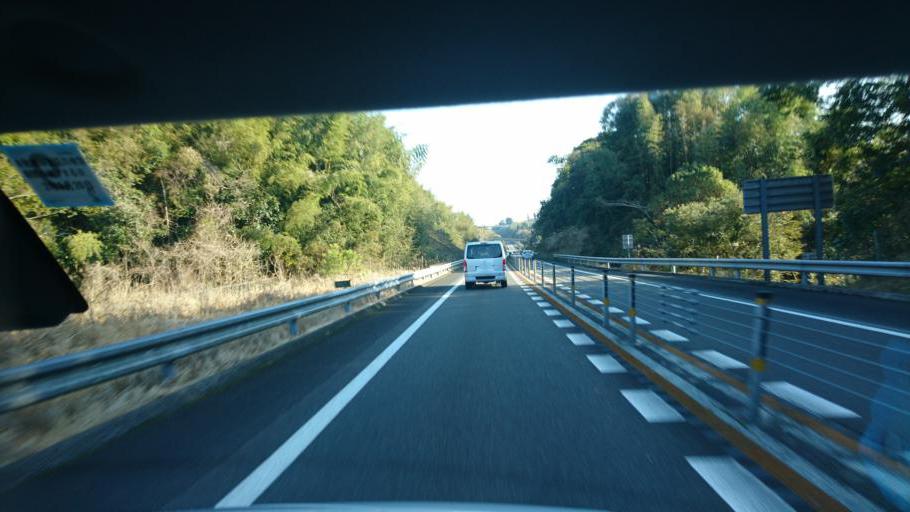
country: JP
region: Miyazaki
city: Tsuma
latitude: 32.0141
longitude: 131.3828
